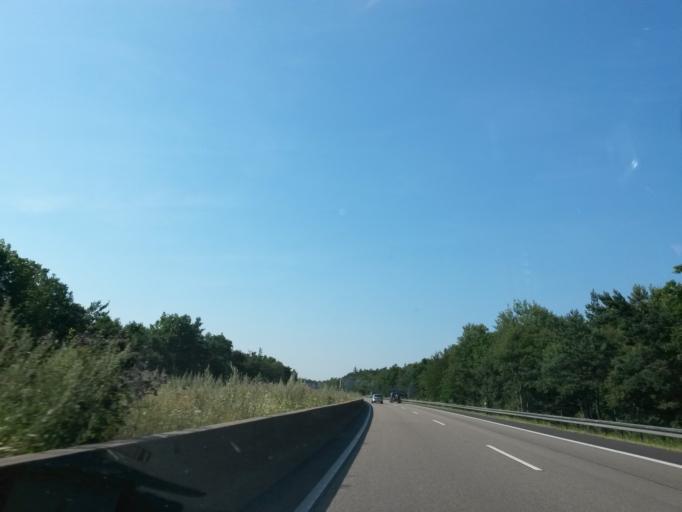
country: DE
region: Hesse
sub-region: Regierungsbezirk Kassel
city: Petersberg
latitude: 50.6156
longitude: 9.6822
